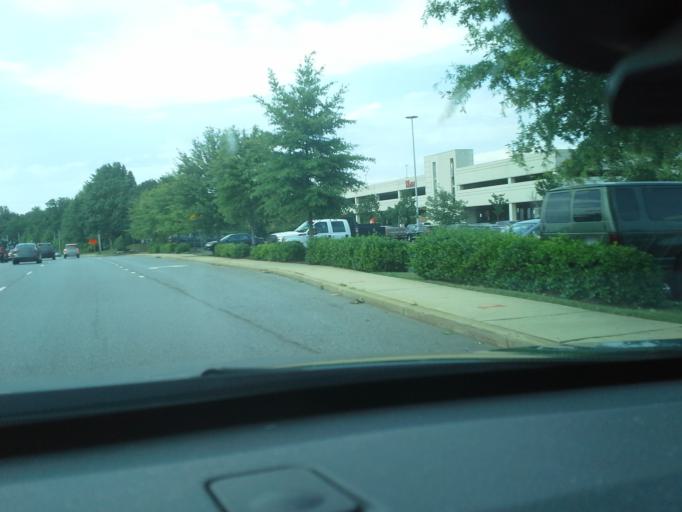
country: US
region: Maryland
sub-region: Anne Arundel County
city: Parole
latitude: 38.9867
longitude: -76.5484
